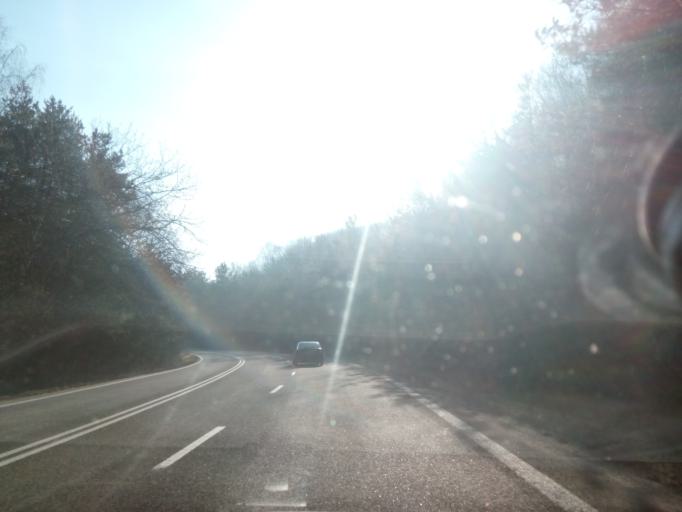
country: SK
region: Kosicky
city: Kosice
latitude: 48.7362
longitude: 21.3708
